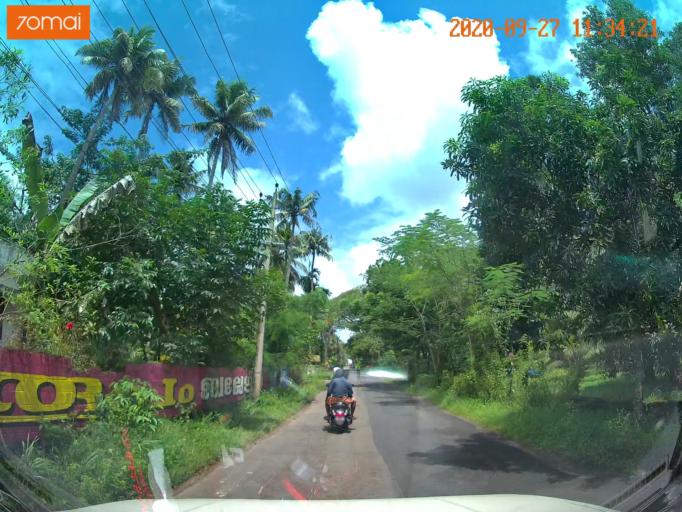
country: IN
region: Kerala
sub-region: Thrissur District
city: Thanniyam
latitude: 10.4363
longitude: 76.1269
